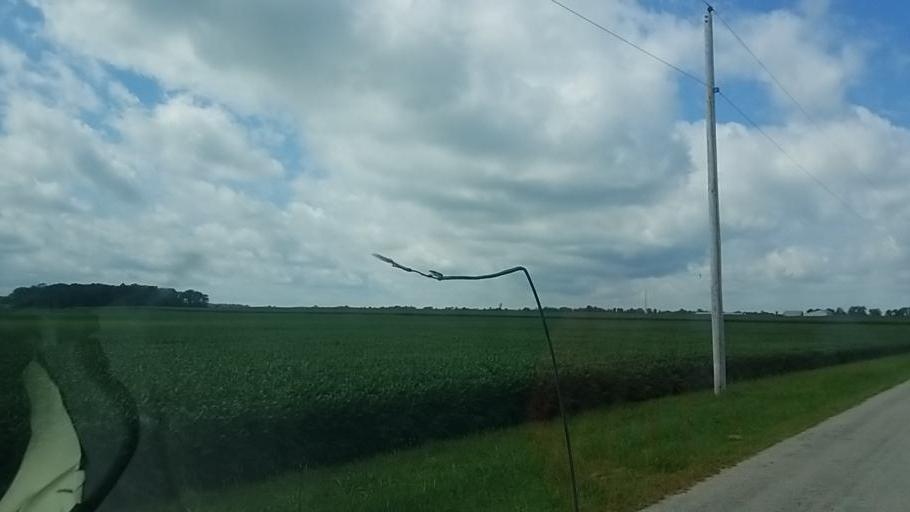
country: US
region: Ohio
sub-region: Madison County
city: Bethel
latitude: 39.7173
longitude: -83.4334
